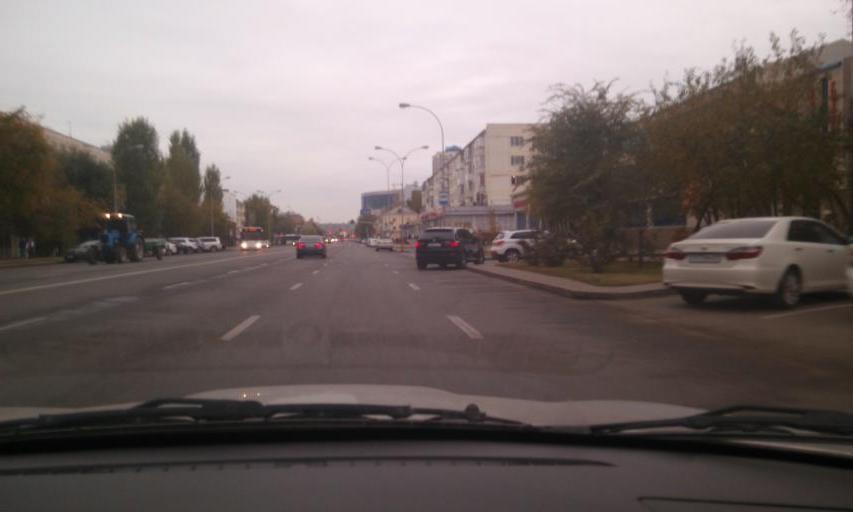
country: KZ
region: Astana Qalasy
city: Astana
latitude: 51.1720
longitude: 71.4121
